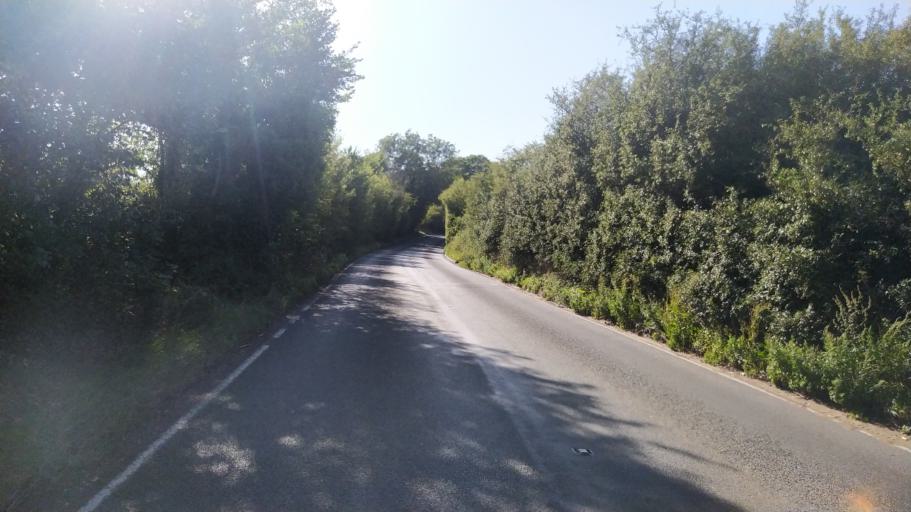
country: GB
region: England
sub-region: Hampshire
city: Kingsley
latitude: 51.1340
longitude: -0.8937
